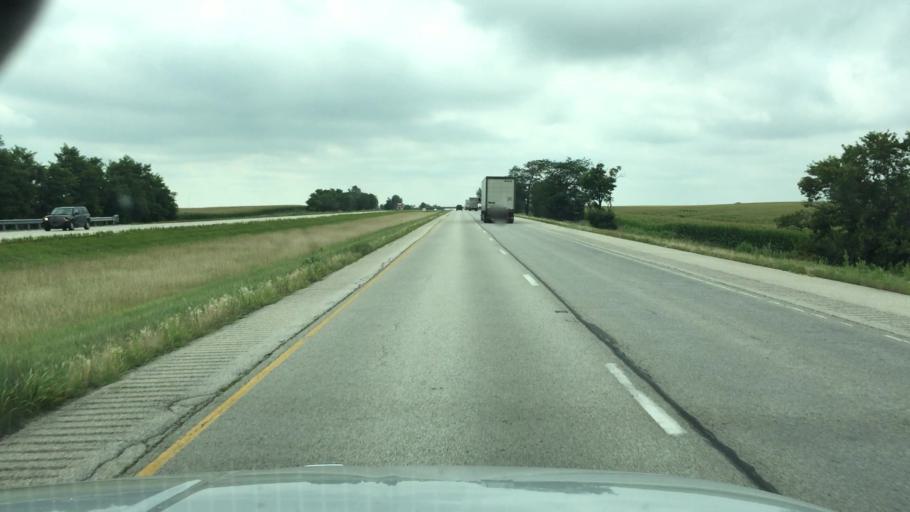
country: US
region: Illinois
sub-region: Knox County
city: Galesburg
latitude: 41.0336
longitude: -90.3346
